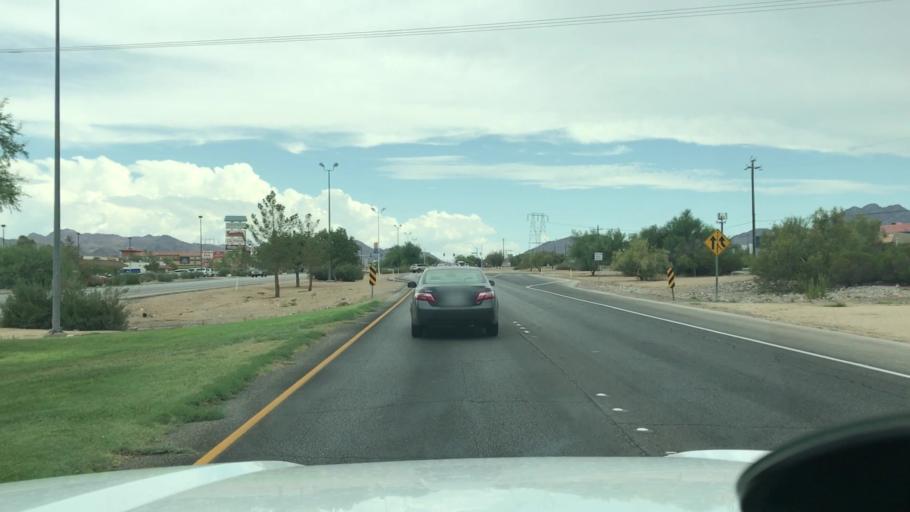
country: US
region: Nevada
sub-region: Clark County
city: Henderson
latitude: 36.0268
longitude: -114.9679
